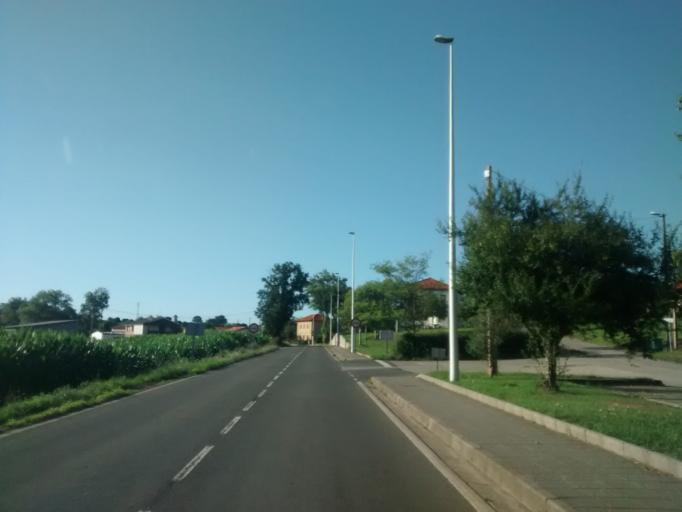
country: ES
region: Cantabria
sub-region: Provincia de Cantabria
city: Lierganes
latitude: 43.4020
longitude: -3.7370
